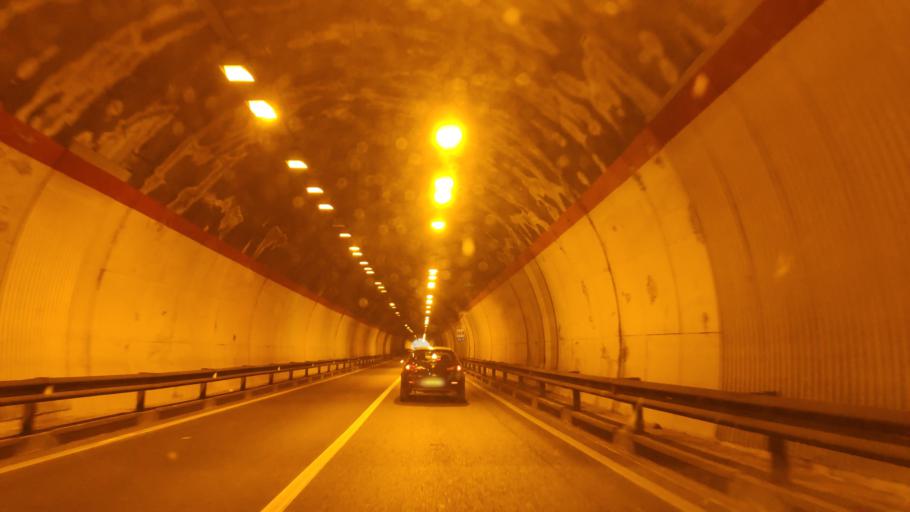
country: IT
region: Calabria
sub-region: Provincia di Cosenza
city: Marina
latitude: 39.4710
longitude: 15.9796
